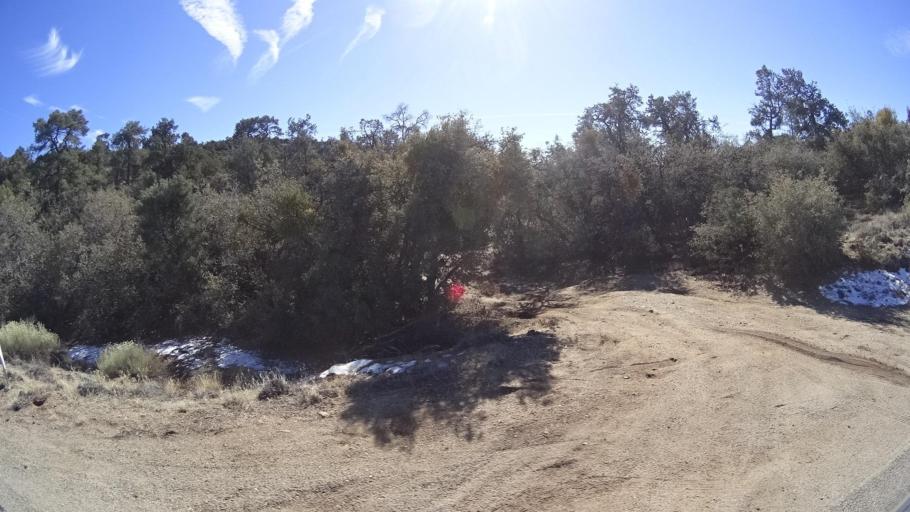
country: US
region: California
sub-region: Kern County
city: Pine Mountain Club
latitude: 34.8665
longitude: -119.2566
